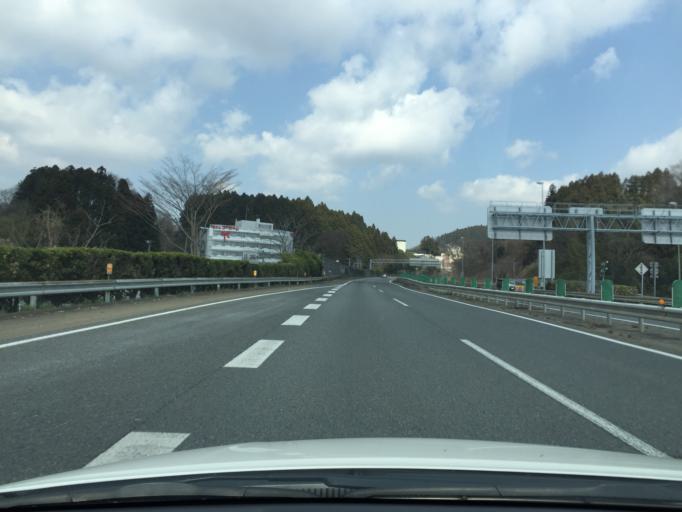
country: JP
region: Miyagi
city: Sendai
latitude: 38.2157
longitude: 140.8029
